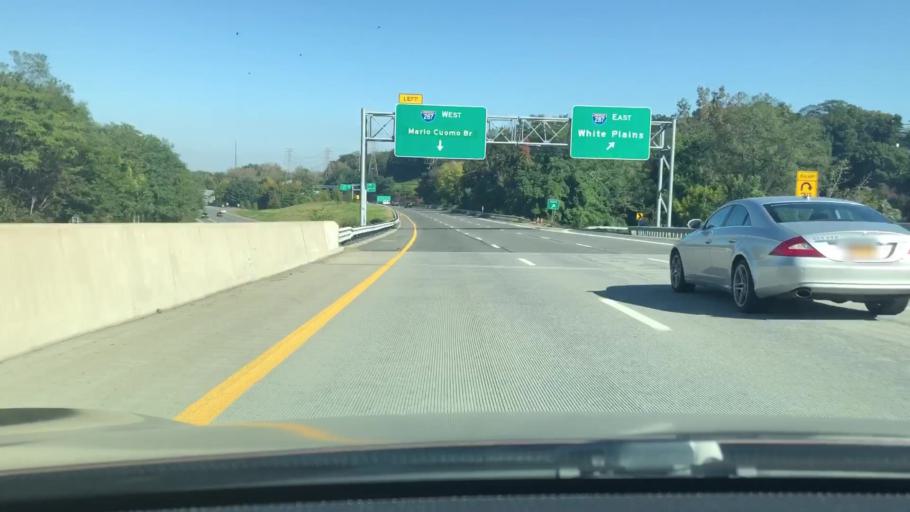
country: US
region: New York
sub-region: Westchester County
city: Elmsford
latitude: 41.0503
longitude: -73.8107
